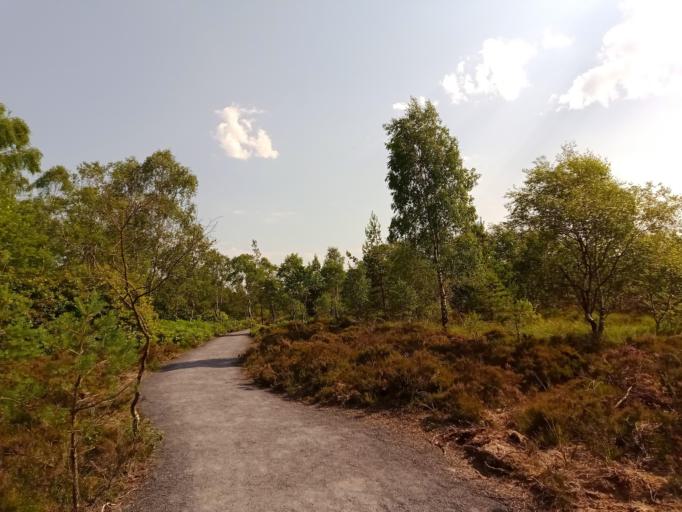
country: IE
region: Leinster
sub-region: Laois
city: Abbeyleix
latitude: 52.8999
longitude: -7.3542
